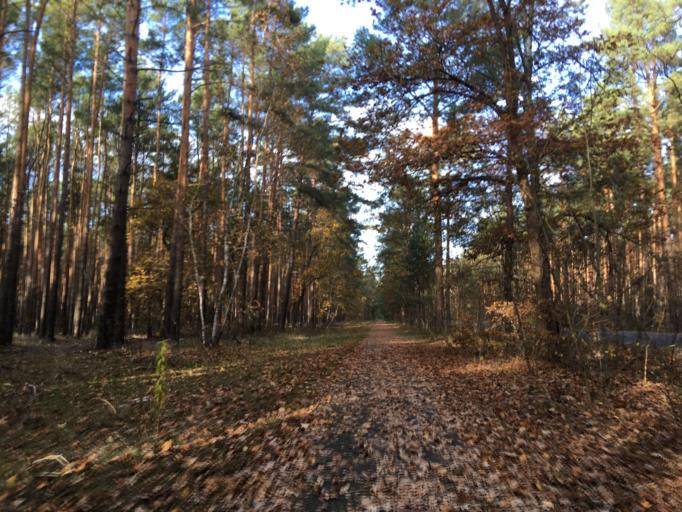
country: DE
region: Brandenburg
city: Gross Koris
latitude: 52.1549
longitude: 13.6753
